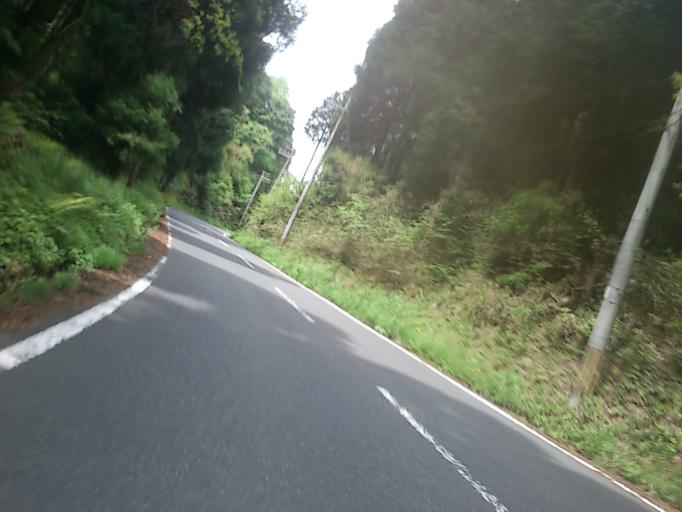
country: JP
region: Kyoto
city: Miyazu
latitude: 35.5870
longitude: 135.1217
